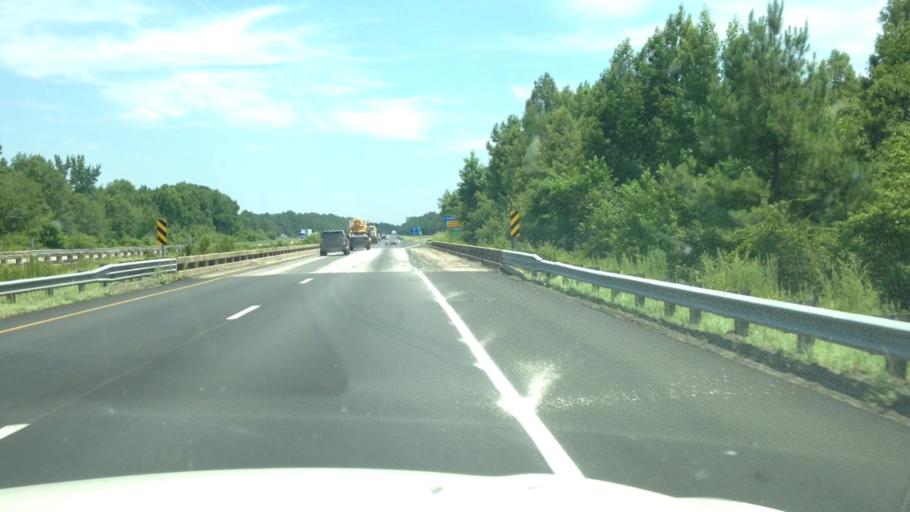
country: US
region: South Carolina
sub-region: Florence County
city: Timmonsville
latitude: 34.2027
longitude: -80.0616
